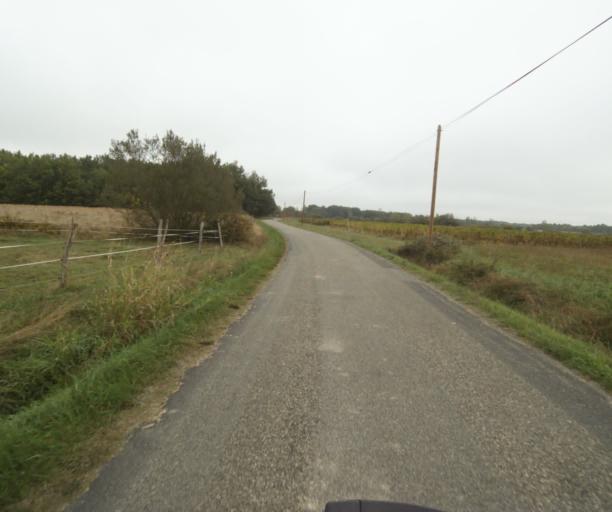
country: FR
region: Midi-Pyrenees
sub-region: Departement du Tarn-et-Garonne
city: Orgueil
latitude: 43.8946
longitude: 1.3894
